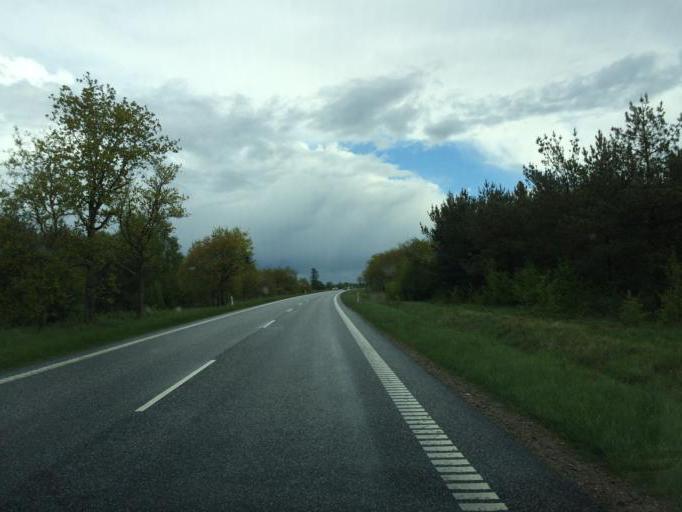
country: DK
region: North Denmark
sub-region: Vesthimmerland Kommune
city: Farso
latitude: 56.6085
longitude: 9.3354
